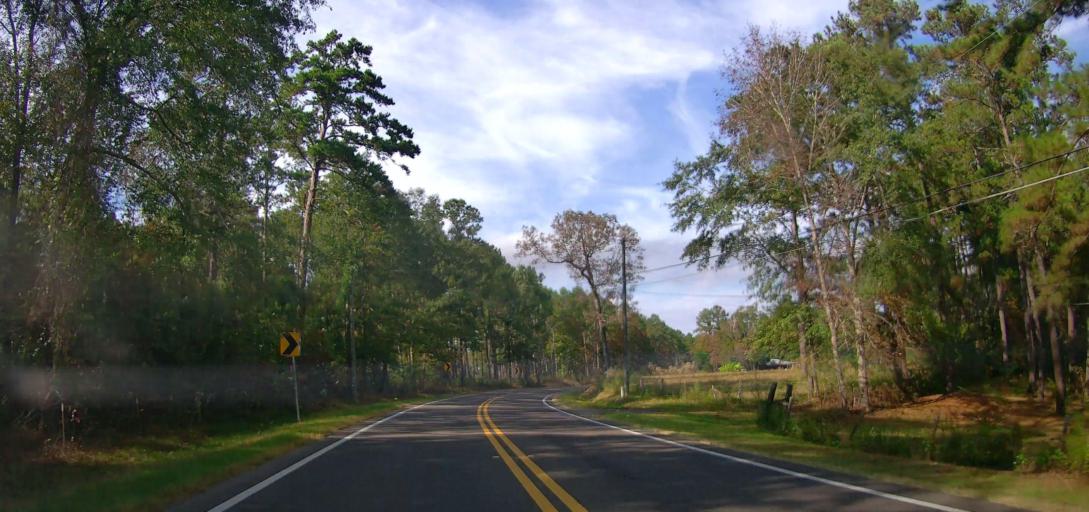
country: US
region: Georgia
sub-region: Thomas County
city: Thomasville
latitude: 30.8761
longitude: -84.0062
